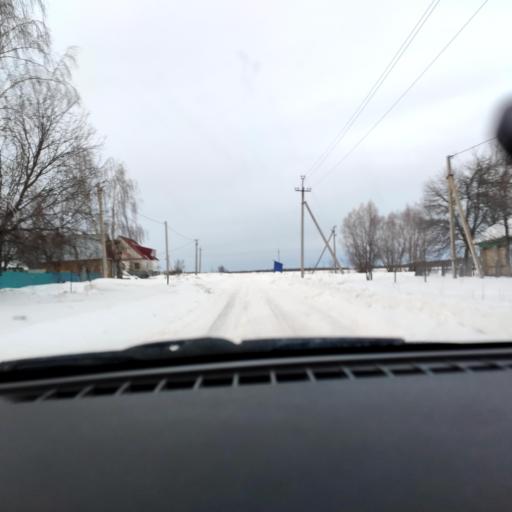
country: RU
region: Bashkortostan
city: Iglino
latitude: 54.7385
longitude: 56.5385
